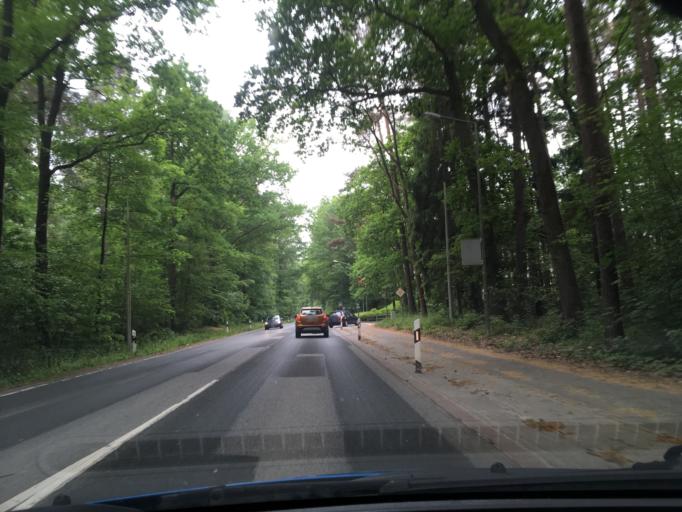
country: DE
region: Lower Saxony
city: Buchholz in der Nordheide
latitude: 53.3400
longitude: 9.8804
